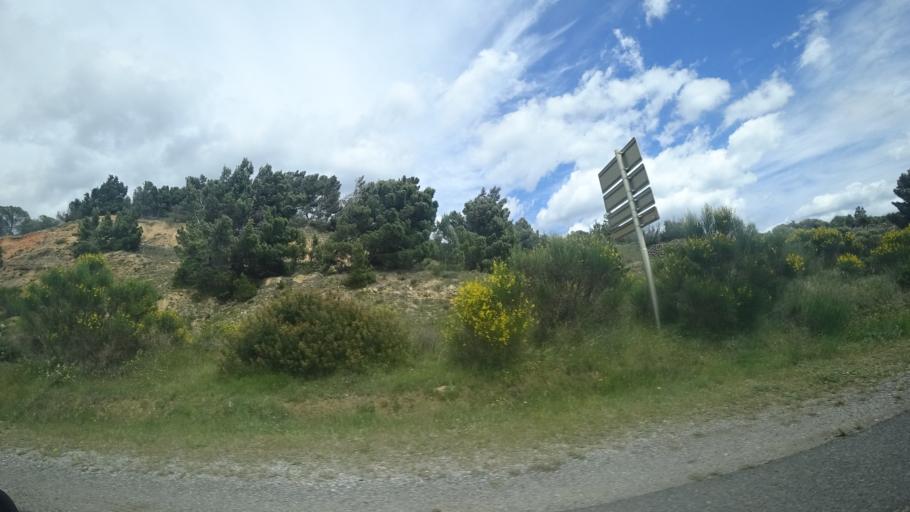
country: FR
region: Languedoc-Roussillon
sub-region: Departement de l'Aude
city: Leucate
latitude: 42.9101
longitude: 3.0208
